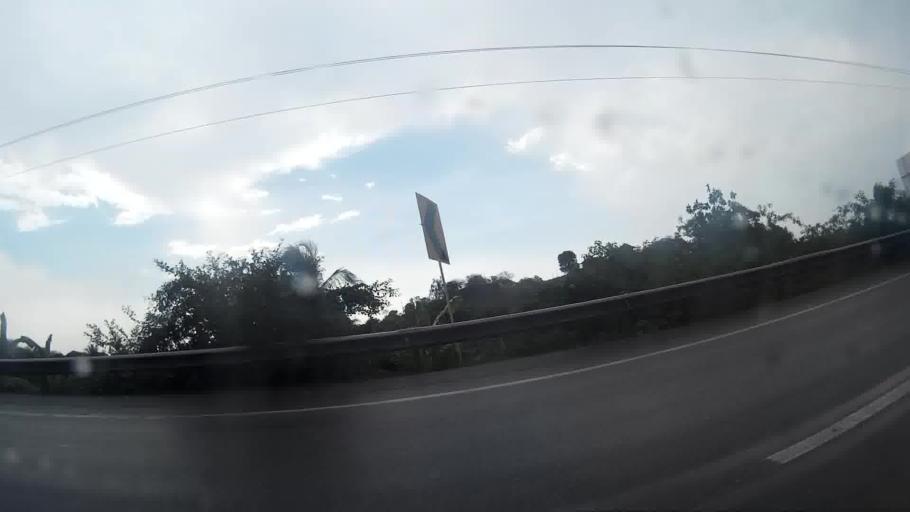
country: CO
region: Magdalena
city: Cienaga
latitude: 11.0166
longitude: -74.2144
